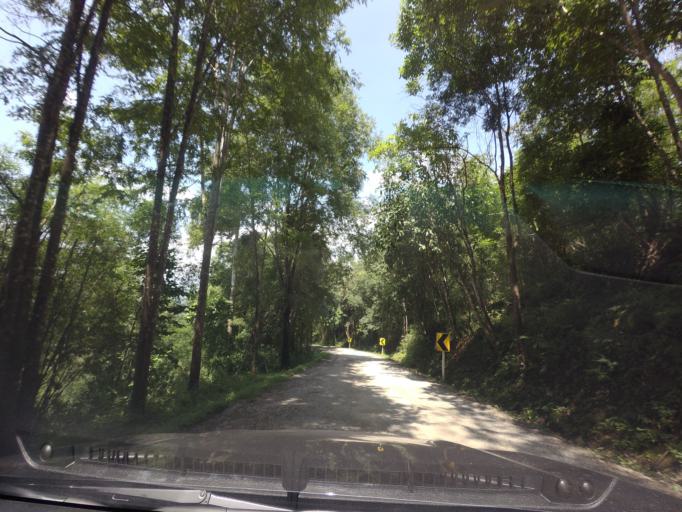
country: TH
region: Loei
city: Na Haeo
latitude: 17.6214
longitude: 100.9000
